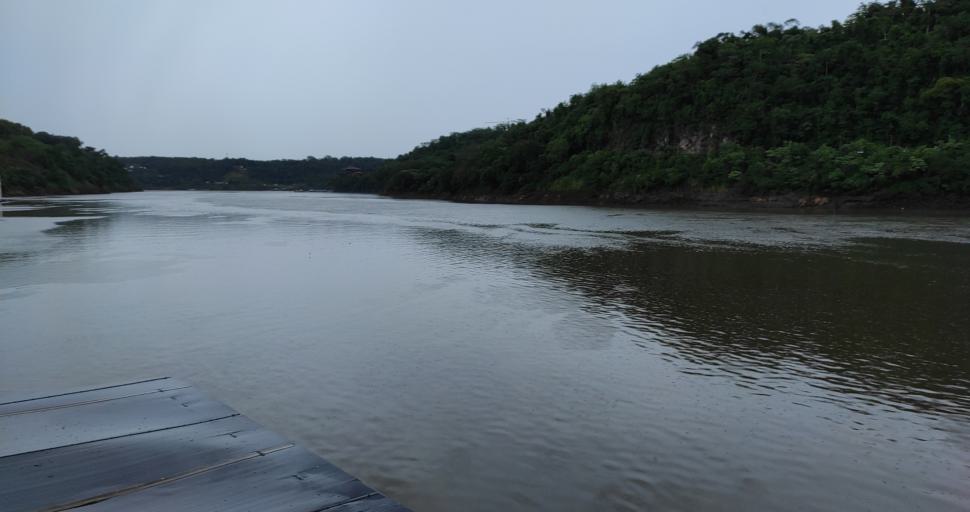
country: AR
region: Misiones
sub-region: Departamento de Iguazu
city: Puerto Iguazu
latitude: -25.5930
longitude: -54.5794
